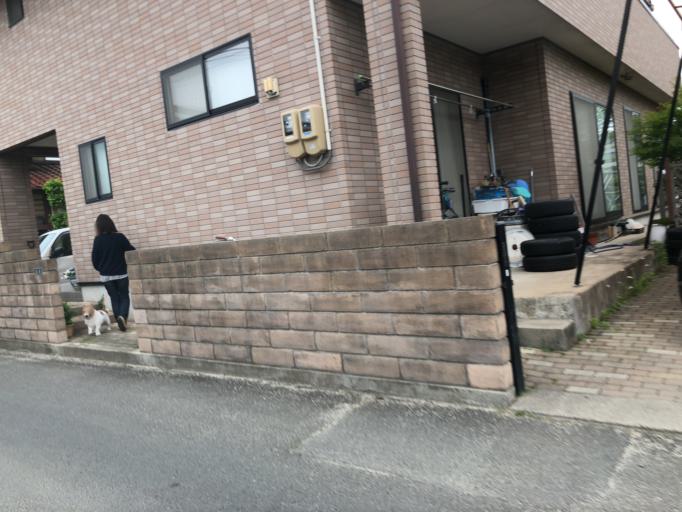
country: JP
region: Fukushima
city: Fukushima-shi
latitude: 37.7942
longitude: 140.4352
